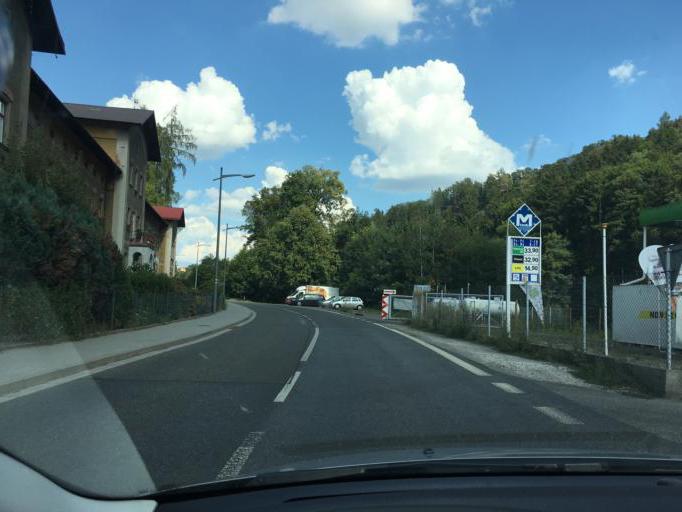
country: CZ
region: Liberecky
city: Semily
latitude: 50.5959
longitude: 15.3455
